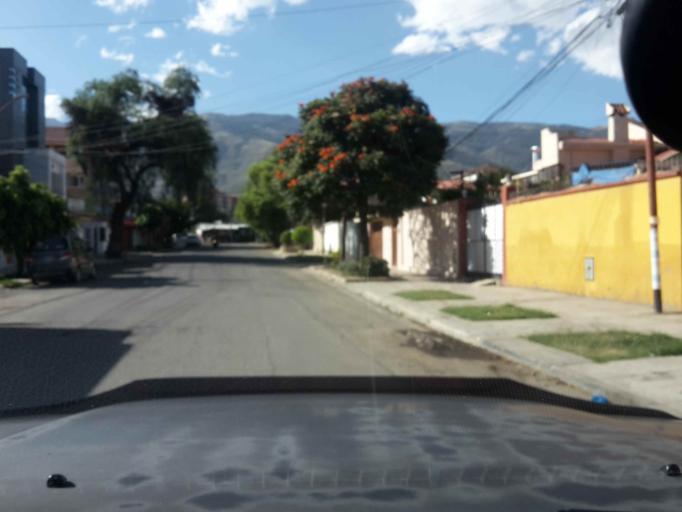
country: BO
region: Cochabamba
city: Cochabamba
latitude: -17.3660
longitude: -66.1775
